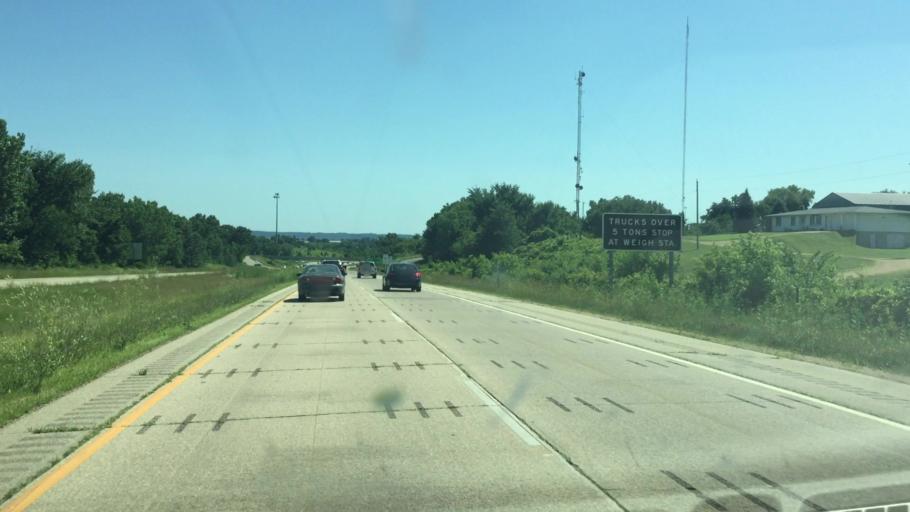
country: US
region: Illinois
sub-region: Jo Daviess County
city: East Dubuque
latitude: 42.5270
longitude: -90.6140
